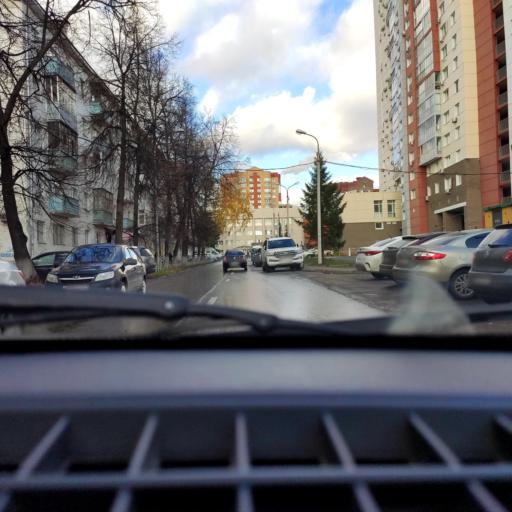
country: RU
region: Bashkortostan
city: Ufa
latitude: 54.7322
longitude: 55.9665
